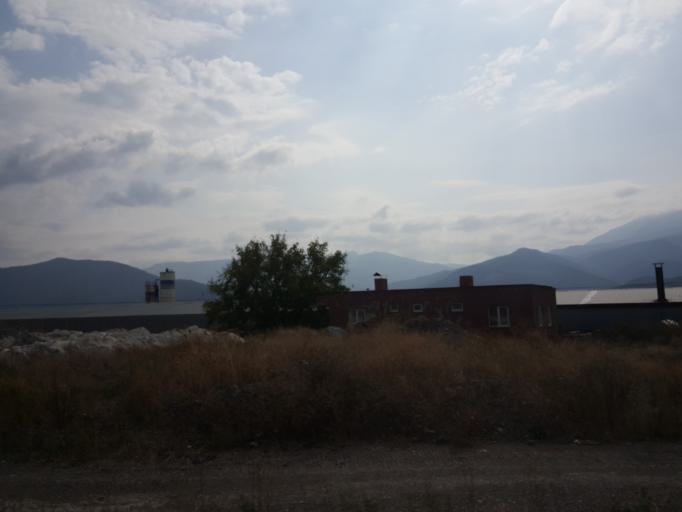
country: TR
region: Corum
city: Hacihamza
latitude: 41.1196
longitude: 34.4087
